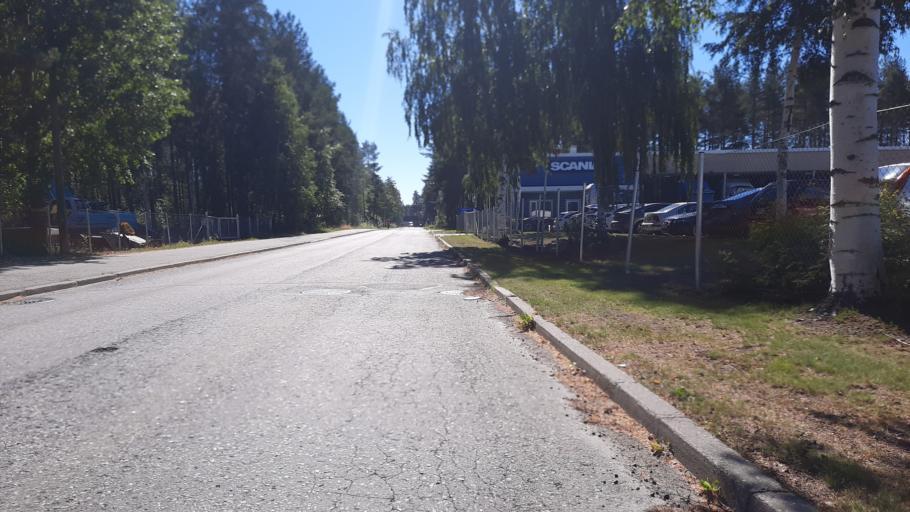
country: FI
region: North Karelia
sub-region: Joensuu
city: Joensuu
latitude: 62.6218
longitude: 29.7432
